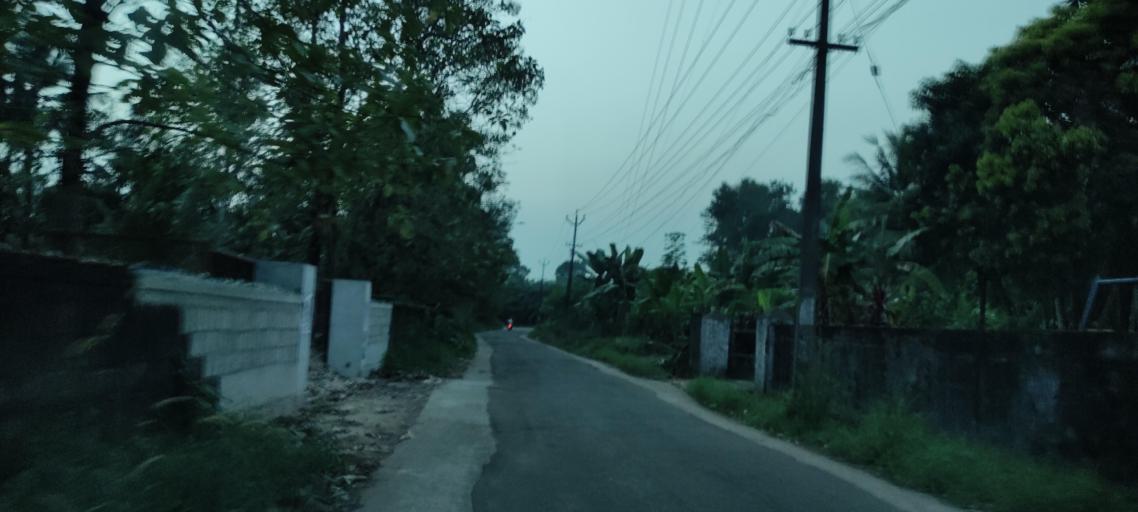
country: IN
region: Kerala
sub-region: Pattanamtitta
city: Adur
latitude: 9.1602
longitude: 76.7402
